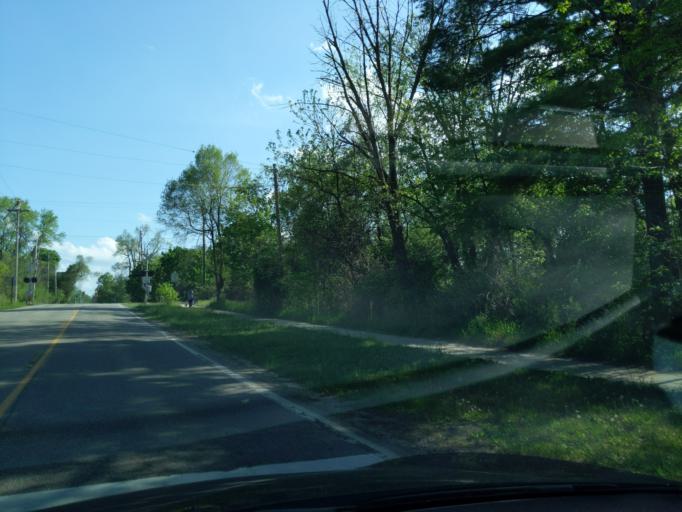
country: US
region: Michigan
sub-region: Ingham County
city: Okemos
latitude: 42.6993
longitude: -84.4104
